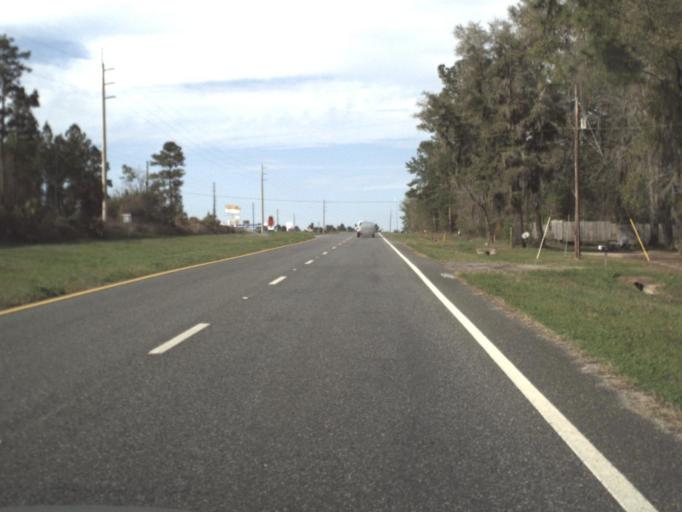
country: US
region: Florida
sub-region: Jefferson County
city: Monticello
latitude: 30.4677
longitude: -83.8916
